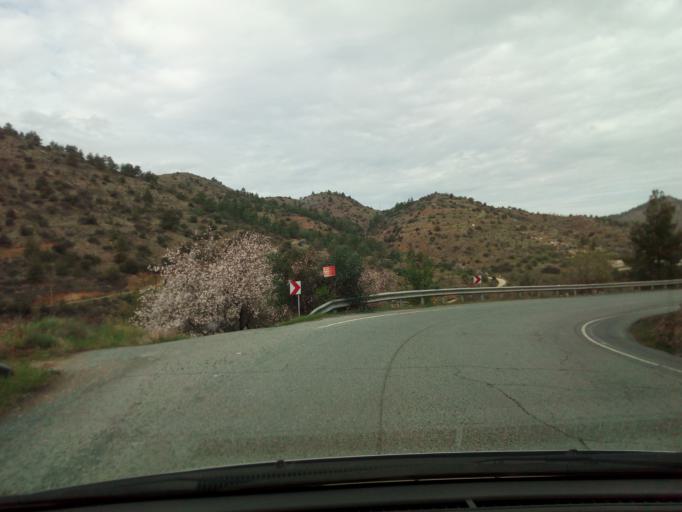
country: CY
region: Lefkosia
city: Klirou
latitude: 34.9600
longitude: 33.1485
